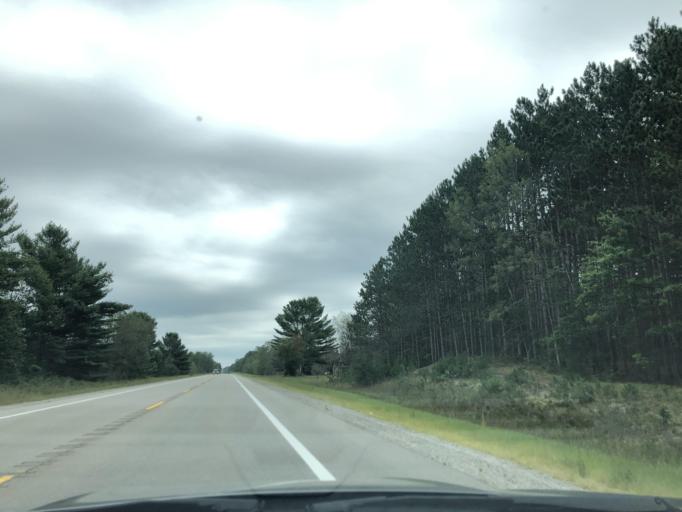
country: US
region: Michigan
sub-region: Clare County
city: Harrison
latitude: 44.0312
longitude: -85.0044
